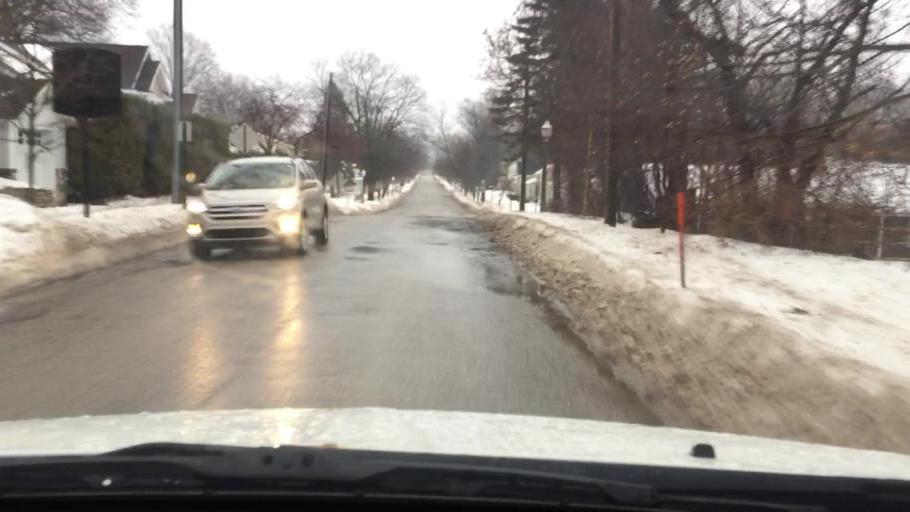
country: US
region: Michigan
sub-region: Charlevoix County
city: Charlevoix
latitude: 45.3153
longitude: -85.2697
